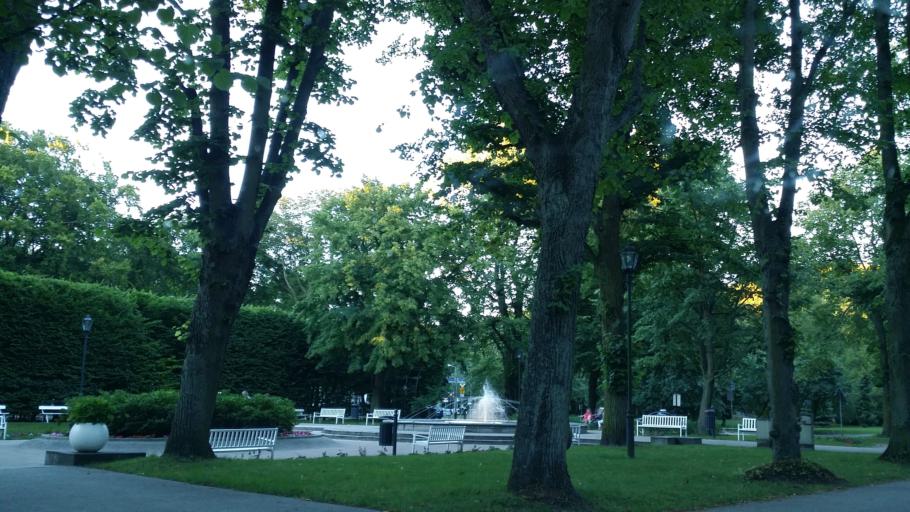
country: PL
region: West Pomeranian Voivodeship
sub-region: Powiat kolobrzeski
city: Kolobrzeg
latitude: 54.1834
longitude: 15.5594
